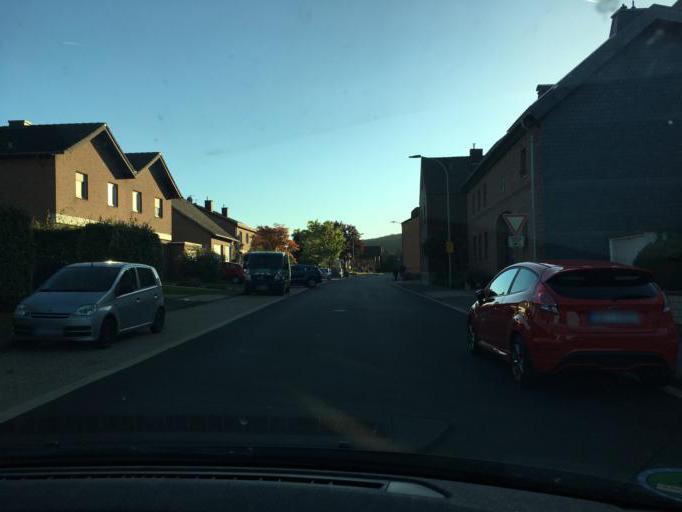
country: DE
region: North Rhine-Westphalia
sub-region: Regierungsbezirk Koln
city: Langerwehe
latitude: 50.8016
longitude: 6.3940
